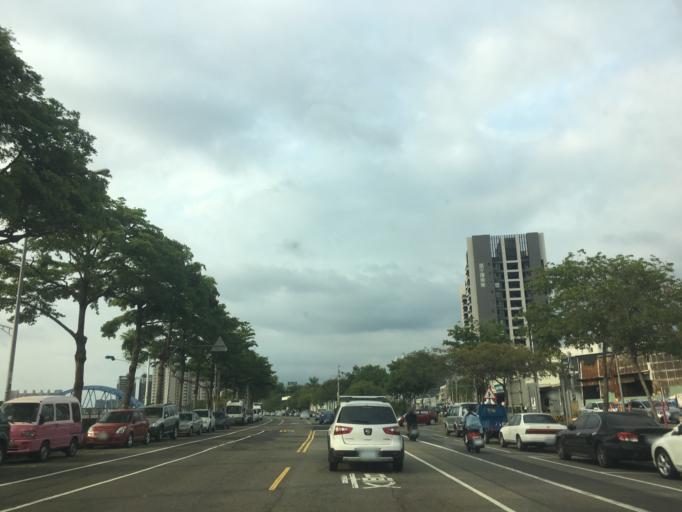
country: TW
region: Taiwan
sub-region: Taichung City
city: Taichung
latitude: 24.1544
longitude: 120.7038
